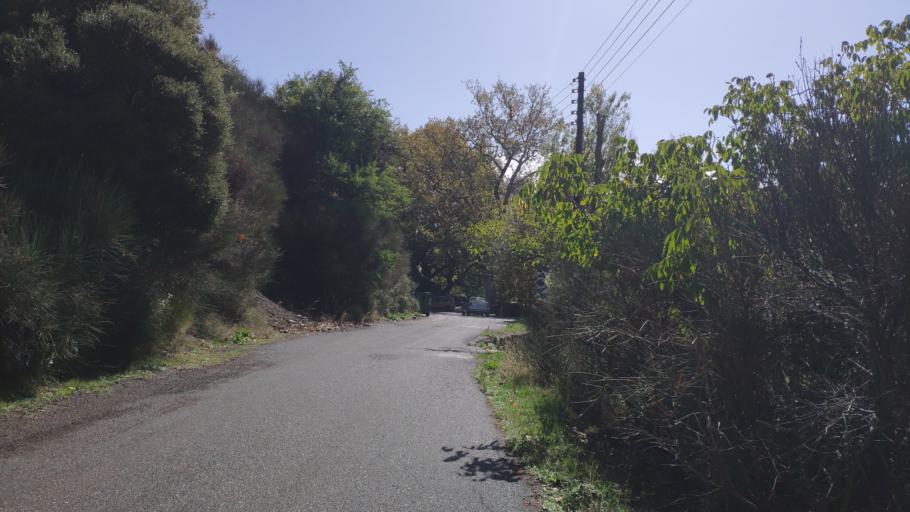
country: GR
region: Peloponnese
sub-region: Nomos Arkadias
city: Dimitsana
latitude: 37.5837
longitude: 22.0472
